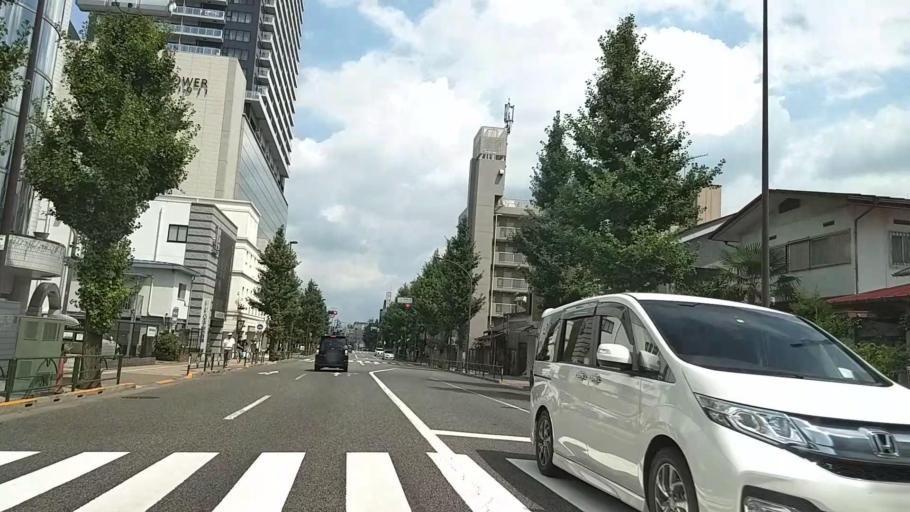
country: JP
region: Tokyo
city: Hachioji
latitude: 35.6543
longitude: 139.3360
